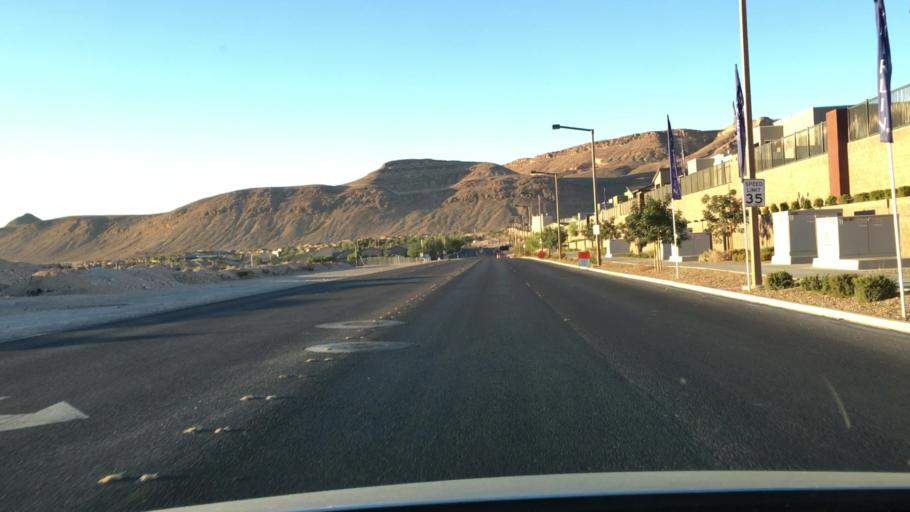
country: US
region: Nevada
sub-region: Clark County
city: Summerlin South
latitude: 36.0733
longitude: -115.3158
